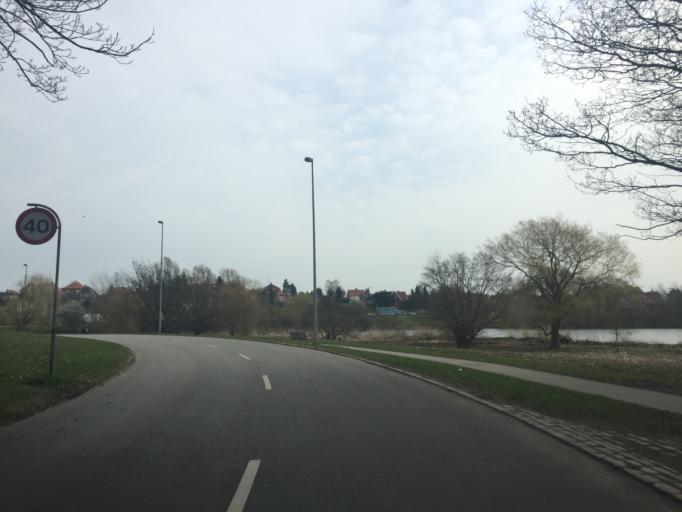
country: DK
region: Capital Region
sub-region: Kobenhavn
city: Vanlose
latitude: 55.7114
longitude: 12.5022
